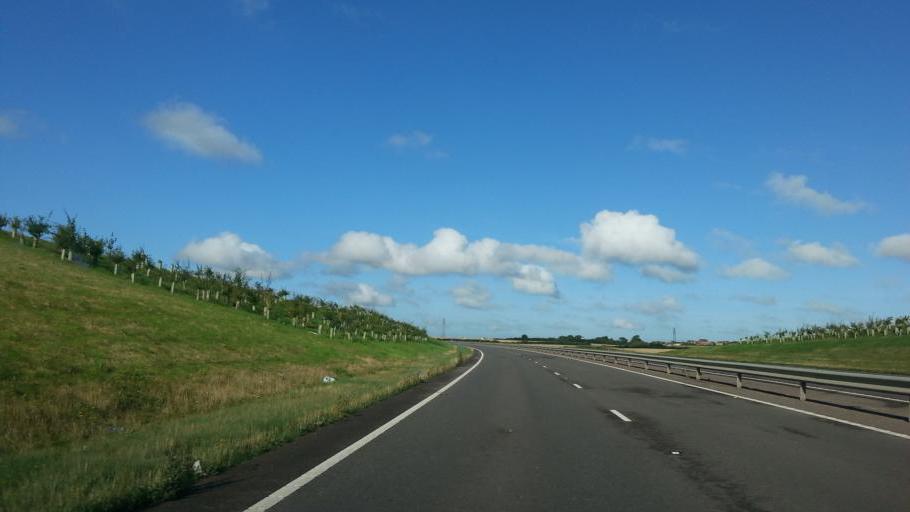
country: GB
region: England
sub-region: Northamptonshire
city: Corby
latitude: 52.4695
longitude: -0.6846
